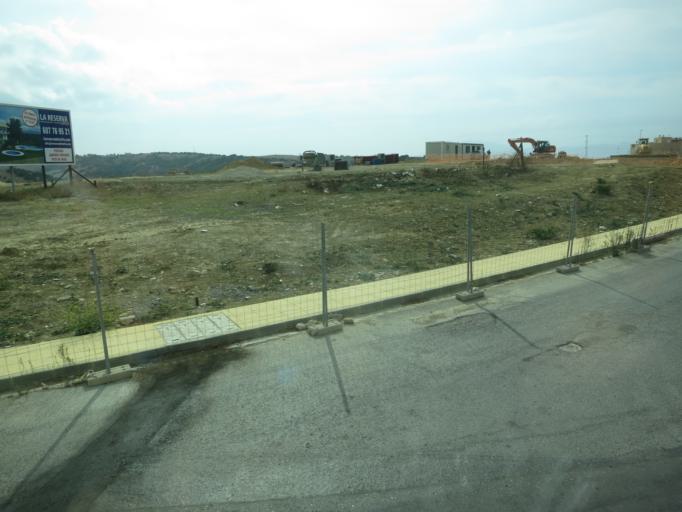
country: ES
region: Andalusia
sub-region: Provincia de Cadiz
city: Tarifa
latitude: 36.0196
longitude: -5.5998
